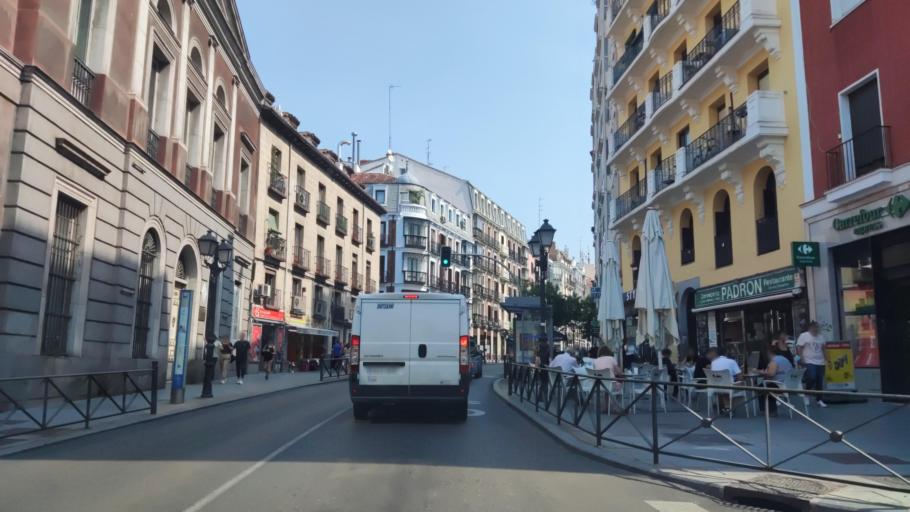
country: ES
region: Madrid
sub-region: Provincia de Madrid
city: City Center
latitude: 40.4251
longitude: -3.7074
